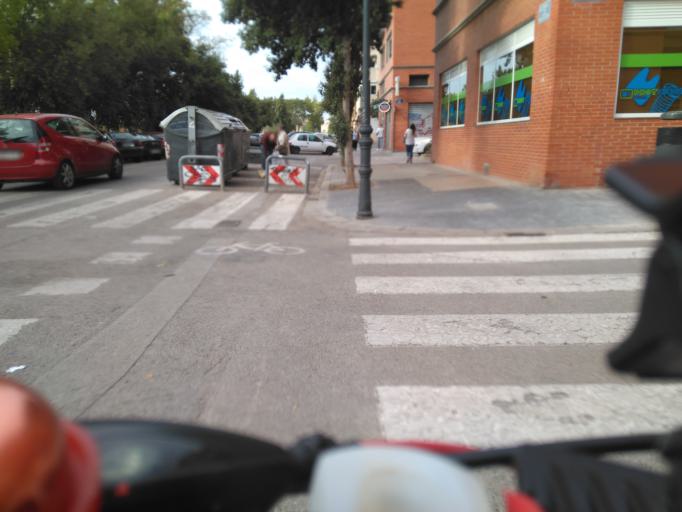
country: ES
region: Valencia
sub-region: Provincia de Valencia
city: Valencia
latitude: 39.4825
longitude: -0.3688
